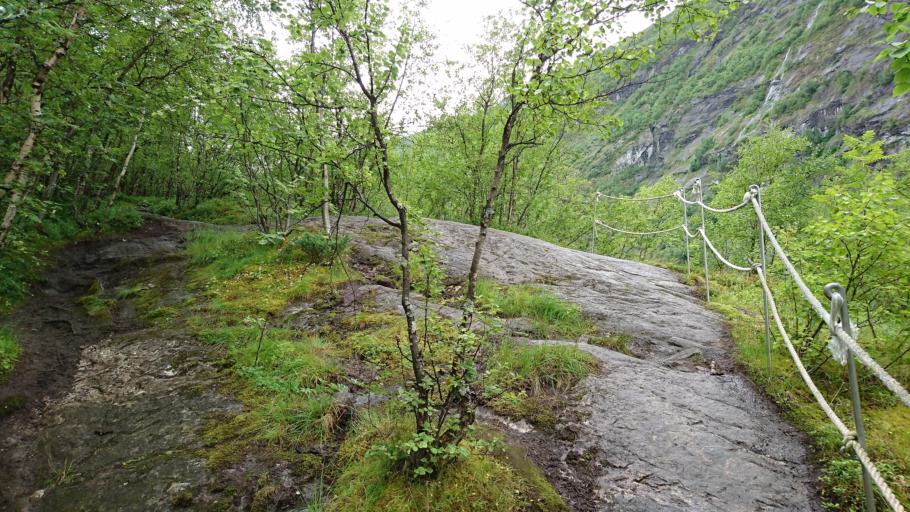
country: NO
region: Sogn og Fjordane
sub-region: Ardal
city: Farnes
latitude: 61.3775
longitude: 7.9299
